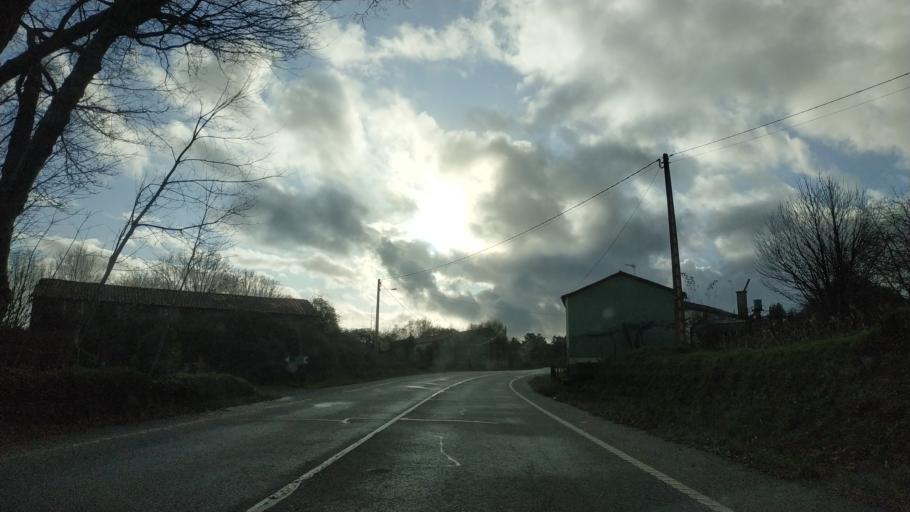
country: ES
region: Galicia
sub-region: Provincia da Coruna
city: Arzua
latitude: 42.8869
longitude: -8.1818
